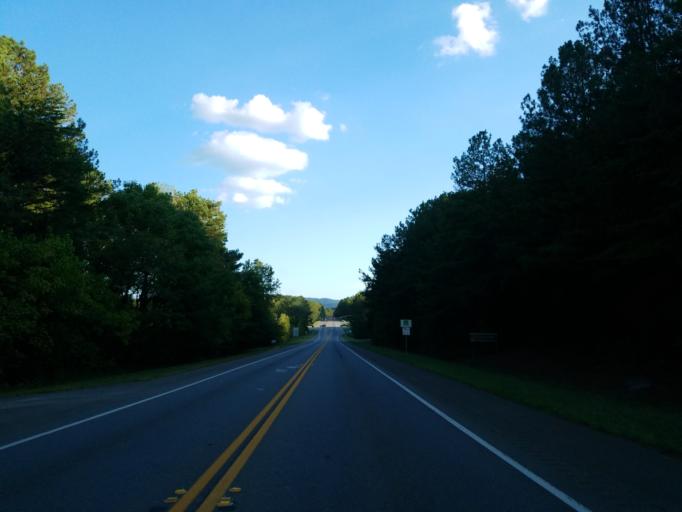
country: US
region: Georgia
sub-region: Murray County
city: Chatsworth
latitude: 34.5920
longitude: -84.7073
